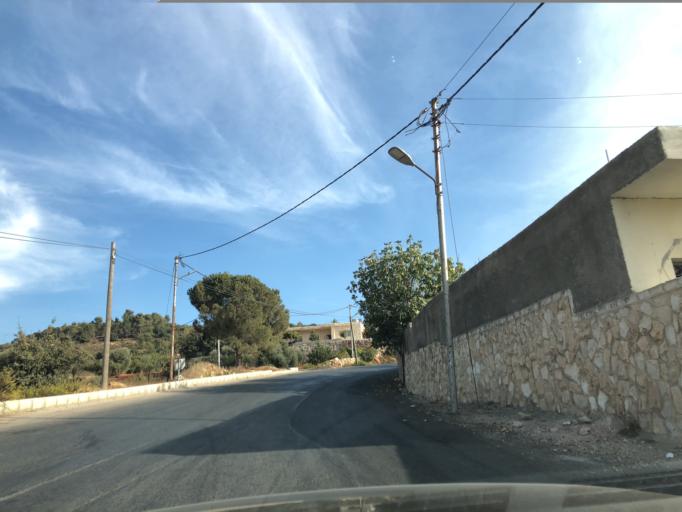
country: JO
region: Irbid
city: `Ayn Jannah
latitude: 32.3281
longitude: 35.7603
